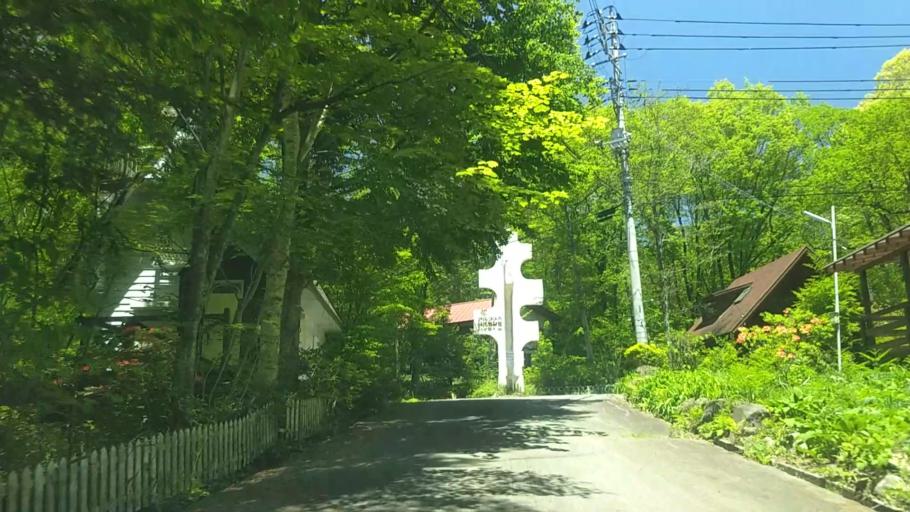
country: JP
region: Yamanashi
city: Nirasaki
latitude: 35.8906
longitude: 138.4341
